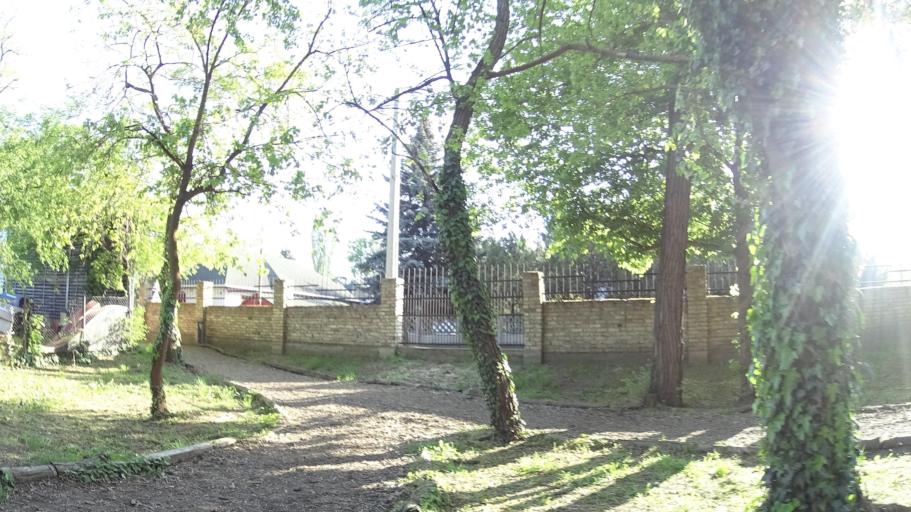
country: HU
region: Budapest
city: Budapest XVIII. keruelet
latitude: 47.4371
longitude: 19.1748
